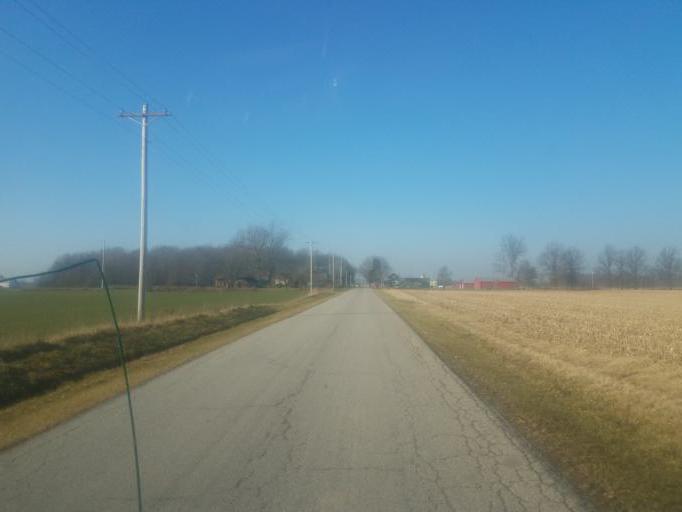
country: US
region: Ohio
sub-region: Seneca County
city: Tiffin
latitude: 41.0371
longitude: -82.9789
